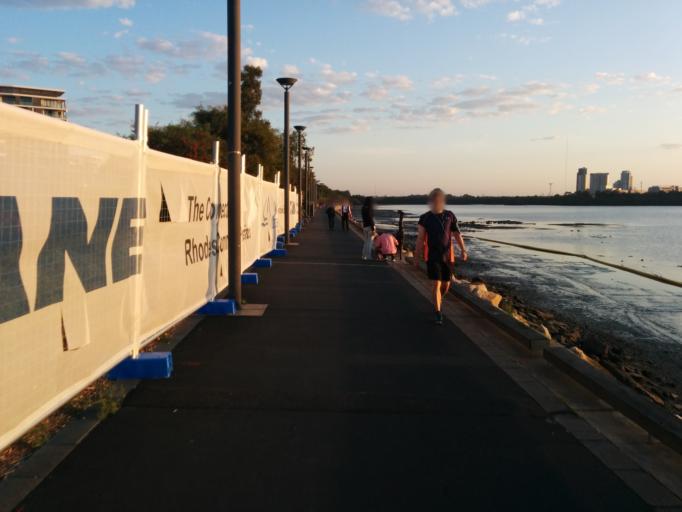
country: AU
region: New South Wales
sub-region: Canada Bay
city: Rhodes
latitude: -33.8294
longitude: 151.0833
